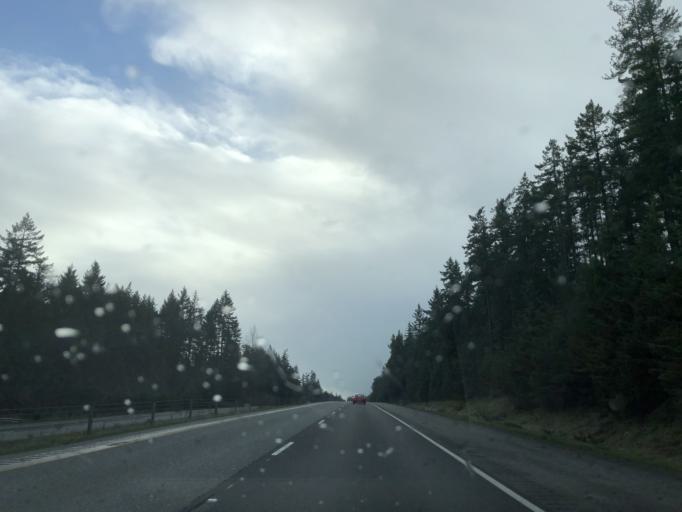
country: US
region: Washington
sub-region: Kitsap County
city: Poulsbo
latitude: 47.7260
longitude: -122.6775
